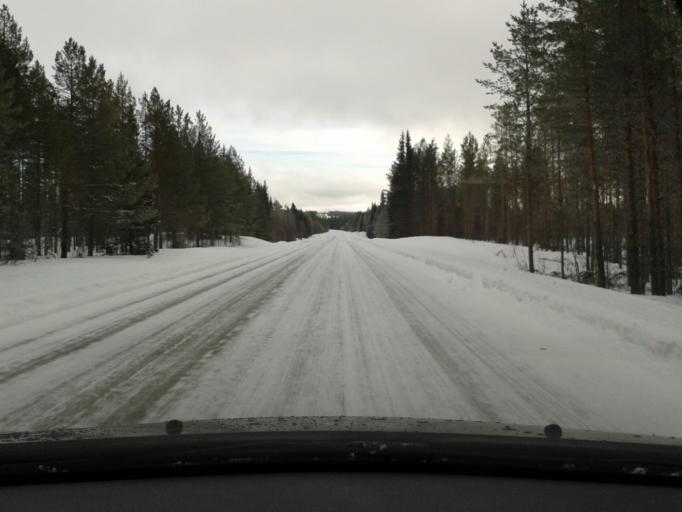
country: SE
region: Vaesterbotten
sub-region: Vilhelmina Kommun
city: Sjoberg
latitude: 64.8064
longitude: 15.9886
